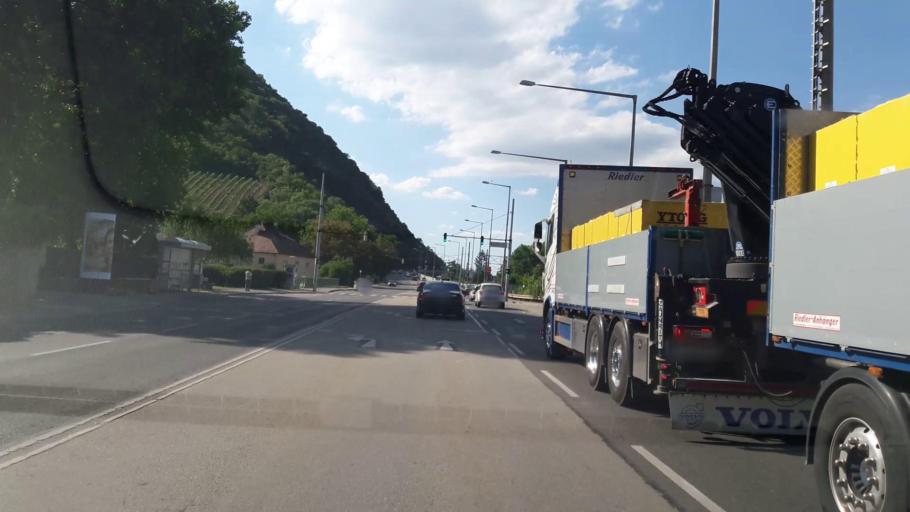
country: AT
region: Lower Austria
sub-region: Politischer Bezirk Korneuburg
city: Langenzersdorf
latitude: 48.2742
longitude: 16.3571
